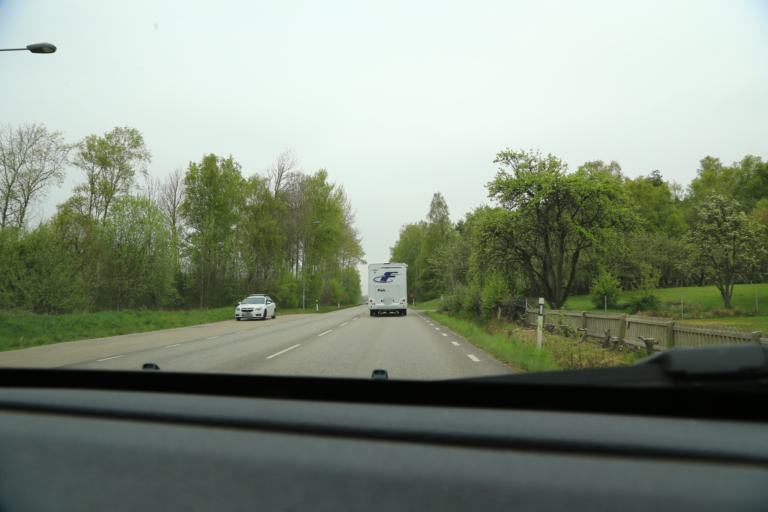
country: SE
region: Halland
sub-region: Varbergs Kommun
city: Varberg
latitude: 57.1762
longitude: 12.2282
